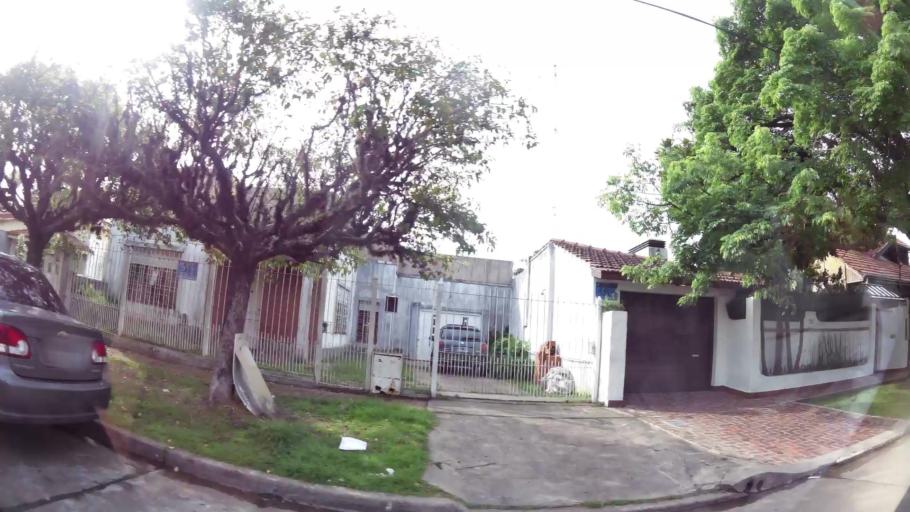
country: AR
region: Buenos Aires
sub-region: Partido de Quilmes
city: Quilmes
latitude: -34.7534
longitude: -58.2785
